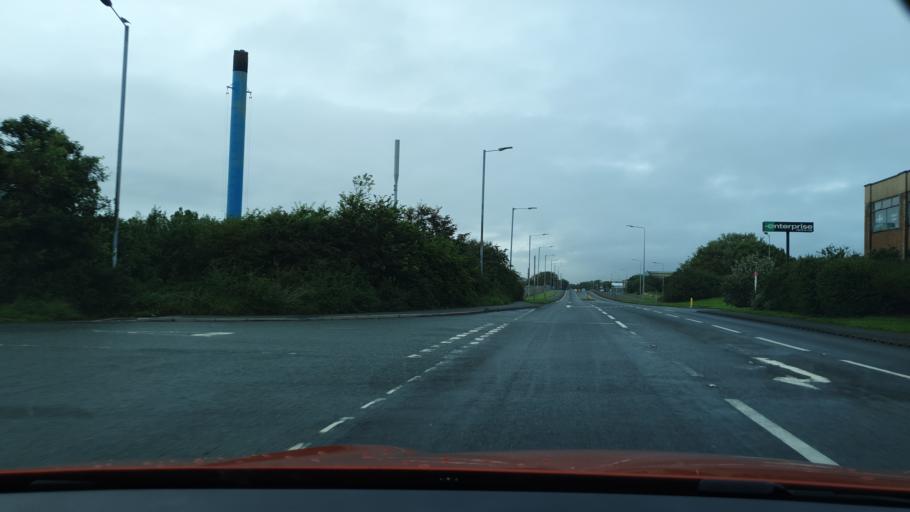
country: GB
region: England
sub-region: Cumbria
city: Barrow in Furness
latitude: 54.1408
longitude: -3.2324
